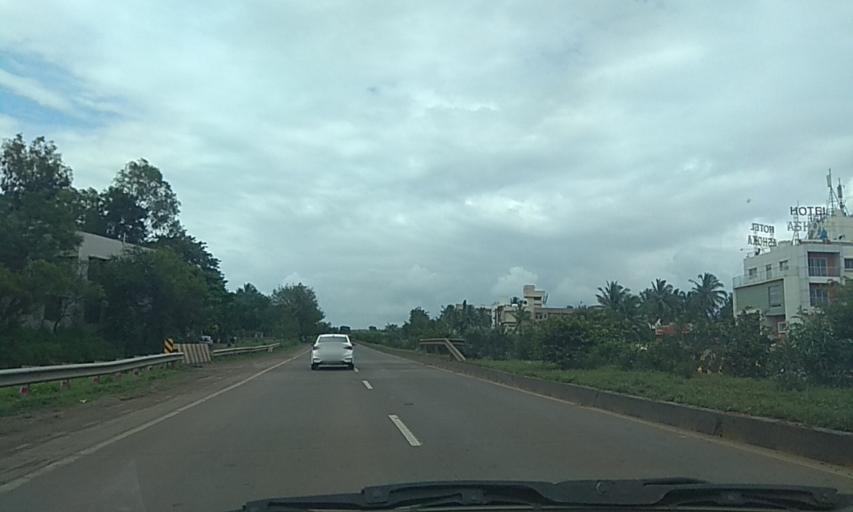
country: IN
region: Maharashtra
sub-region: Kolhapur
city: Kagal
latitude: 16.5865
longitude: 74.3091
